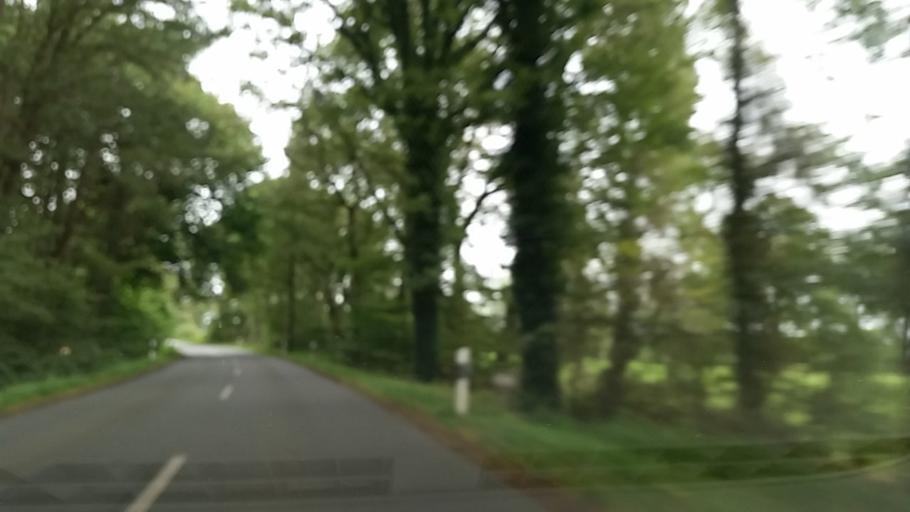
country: DE
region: Lower Saxony
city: Hipstedt
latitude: 53.4193
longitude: 8.9113
